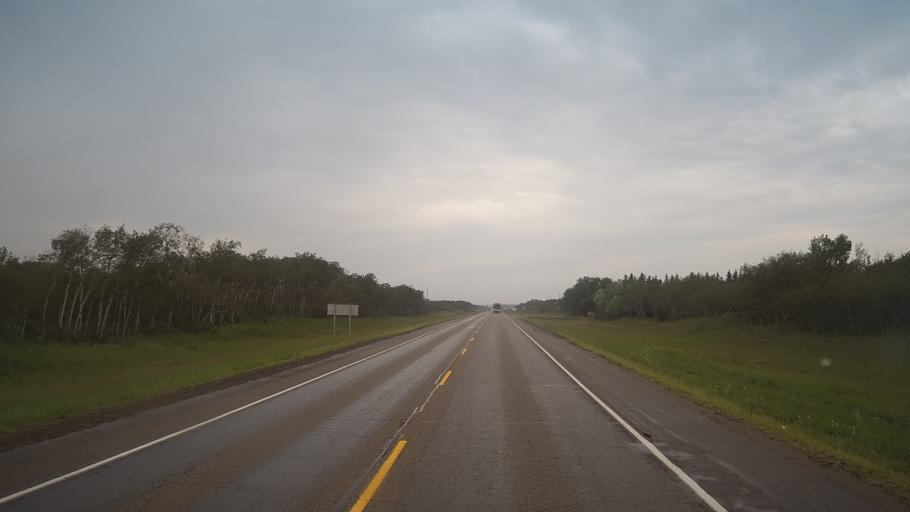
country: CA
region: Saskatchewan
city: Langham
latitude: 52.1294
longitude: -107.0436
